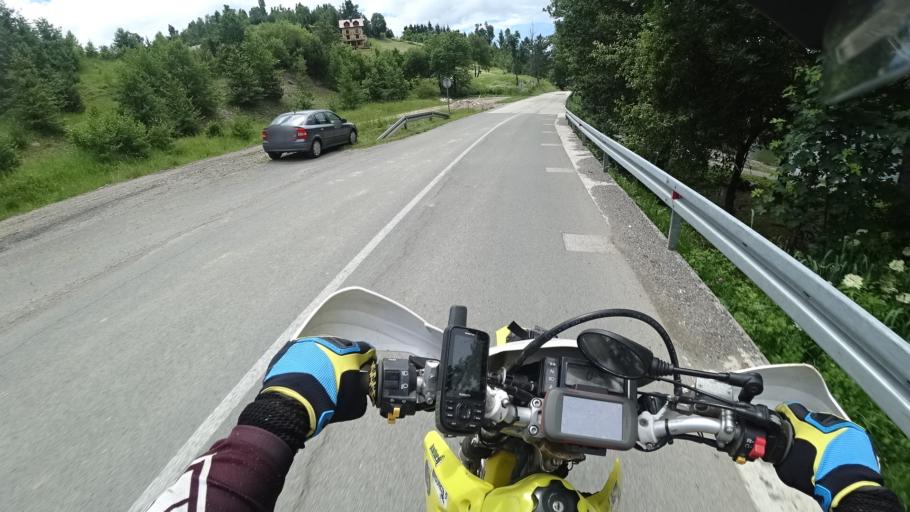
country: HR
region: Primorsko-Goranska
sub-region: Grad Delnice
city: Delnice
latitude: 45.3133
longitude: 14.7180
